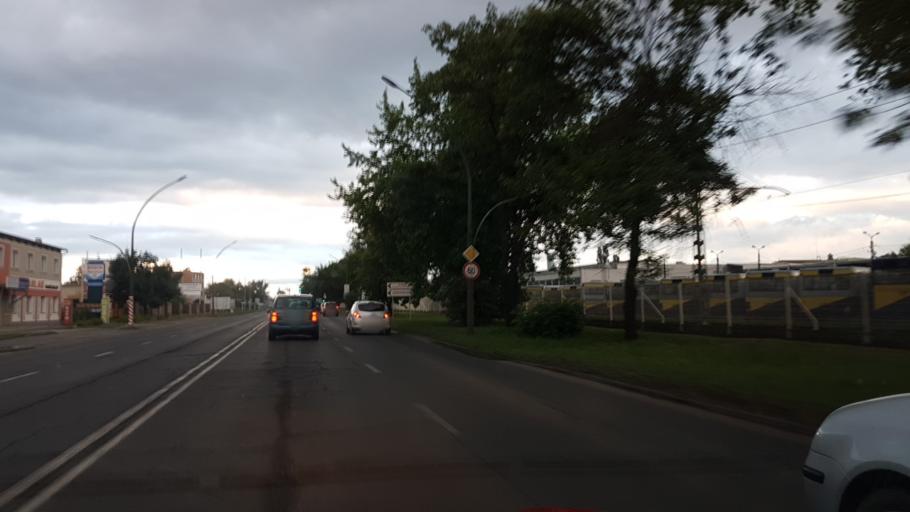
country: HU
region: Borsod-Abauj-Zemplen
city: Miskolc
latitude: 48.1065
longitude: 20.8145
